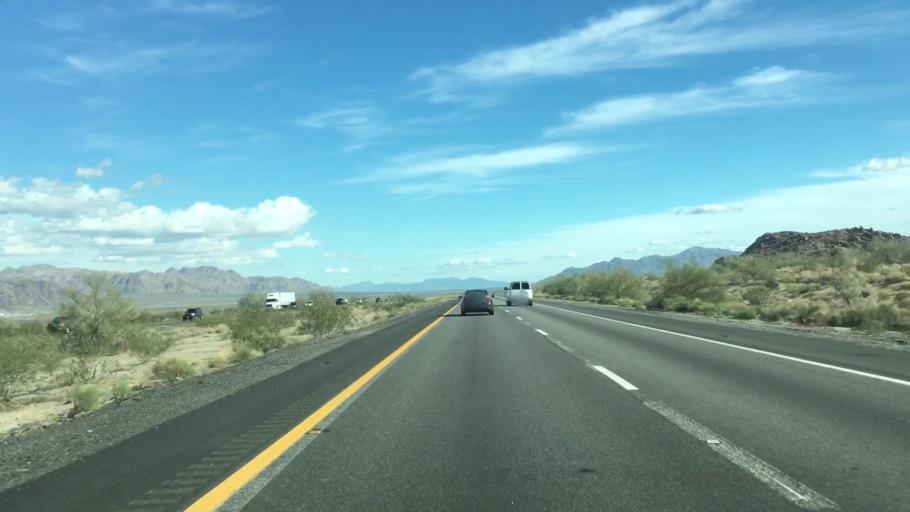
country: US
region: California
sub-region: Riverside County
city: Mecca
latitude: 33.6650
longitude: -115.6897
